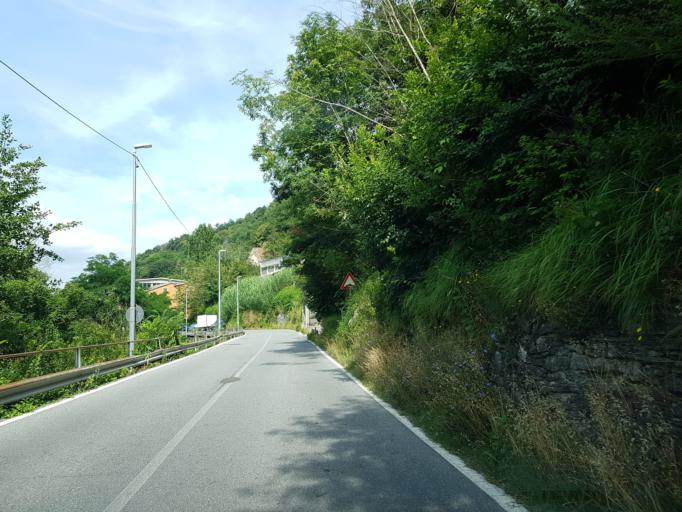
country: IT
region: Liguria
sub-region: Provincia di Genova
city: Piccarello
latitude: 44.4838
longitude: 8.9604
